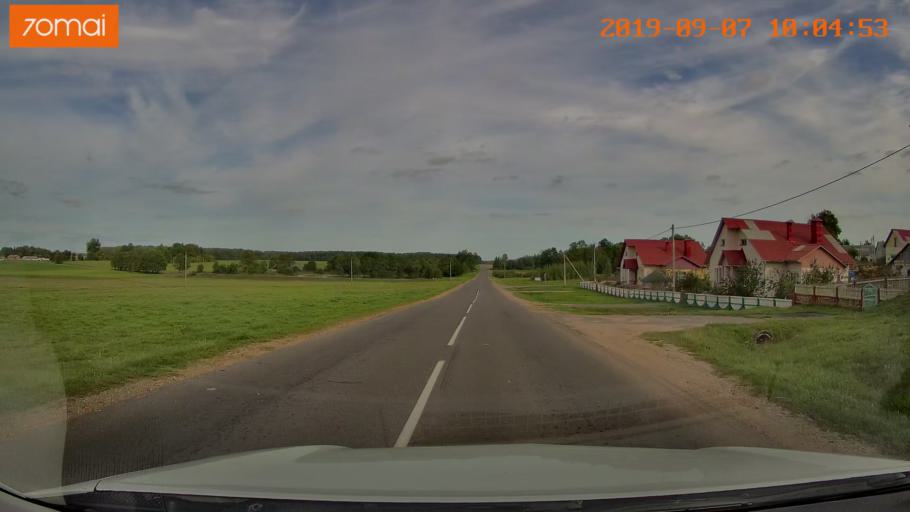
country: BY
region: Grodnenskaya
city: Voranava
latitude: 54.0406
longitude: 25.4101
